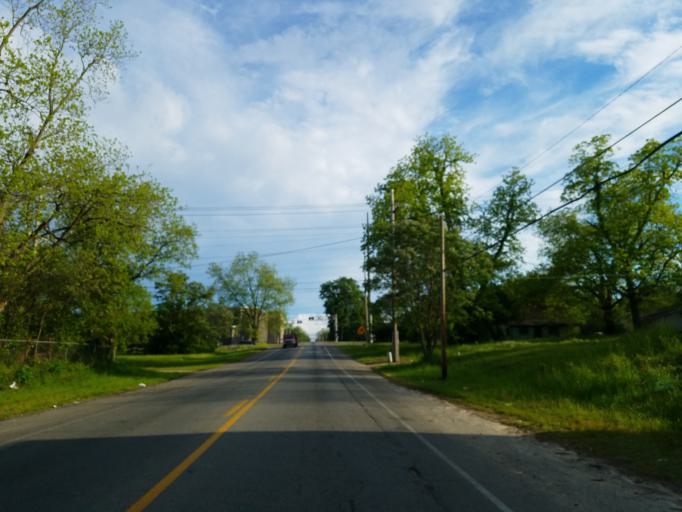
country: US
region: Georgia
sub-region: Crisp County
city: Cordele
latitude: 31.9716
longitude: -83.7881
